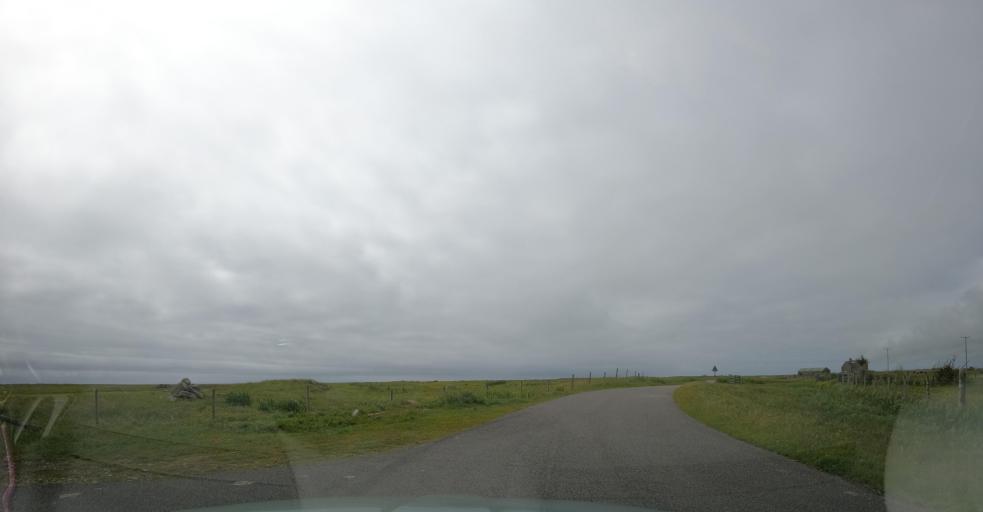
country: GB
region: Scotland
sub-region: Eilean Siar
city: Isle of North Uist
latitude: 57.5278
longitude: -7.3627
